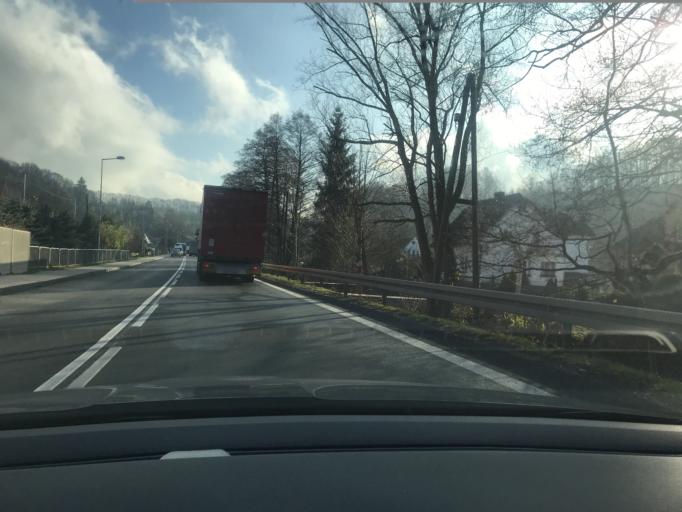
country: PL
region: Lower Silesian Voivodeship
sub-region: Powiat klodzki
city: Kudowa-Zdroj
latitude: 50.4198
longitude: 16.2599
